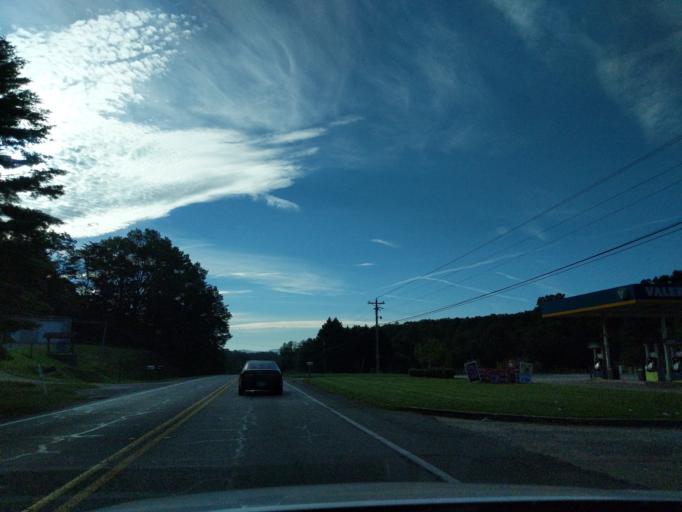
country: US
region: Georgia
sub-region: Fannin County
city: Blue Ridge
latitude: 34.8971
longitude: -84.3614
